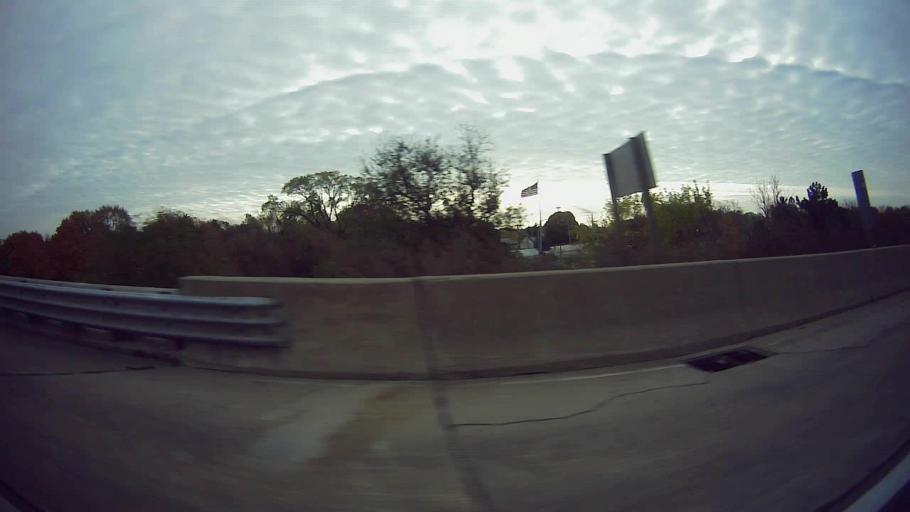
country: US
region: Michigan
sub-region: Wayne County
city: Southgate
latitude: 42.2075
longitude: -83.2294
